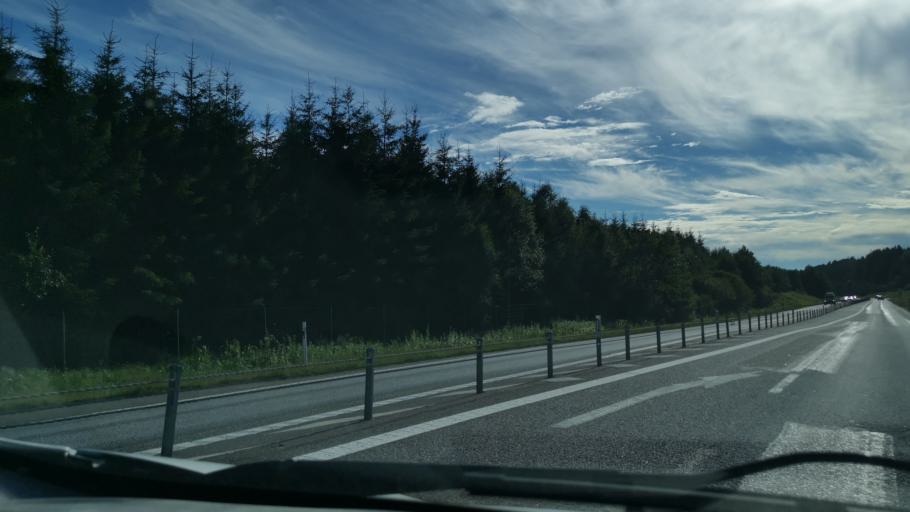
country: SE
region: Vaestra Goetaland
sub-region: Orust
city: Henan
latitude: 58.3506
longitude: 11.7234
